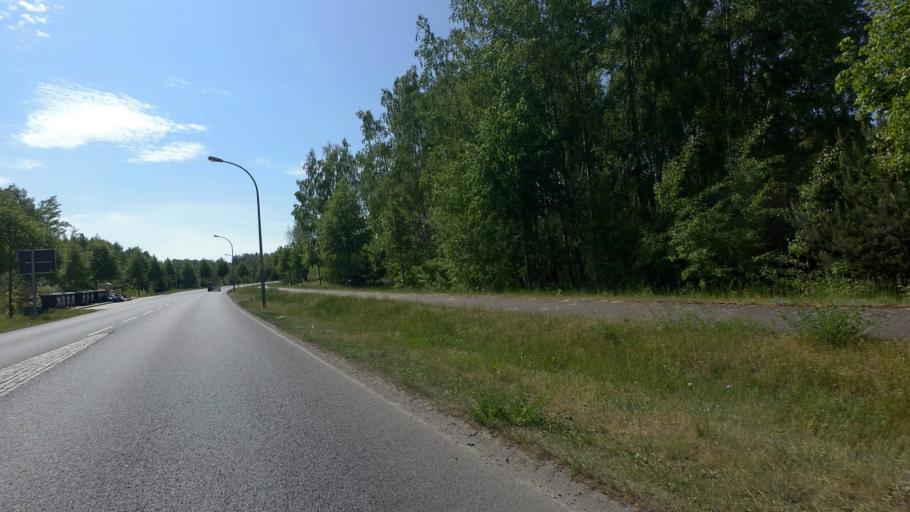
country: DE
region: Brandenburg
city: Leegebruch
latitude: 52.7240
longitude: 13.2273
